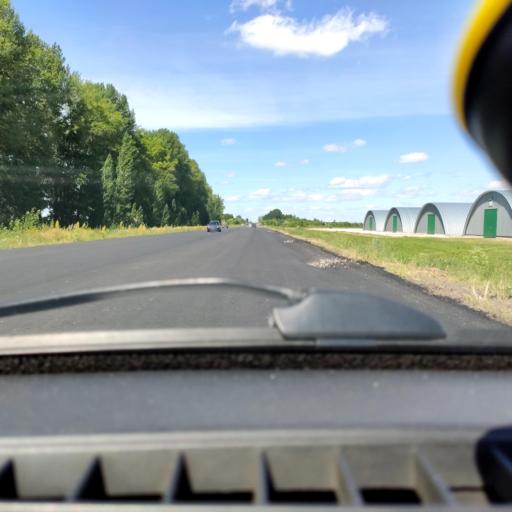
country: RU
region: Samara
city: Tol'yatti
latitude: 53.6886
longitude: 49.4178
